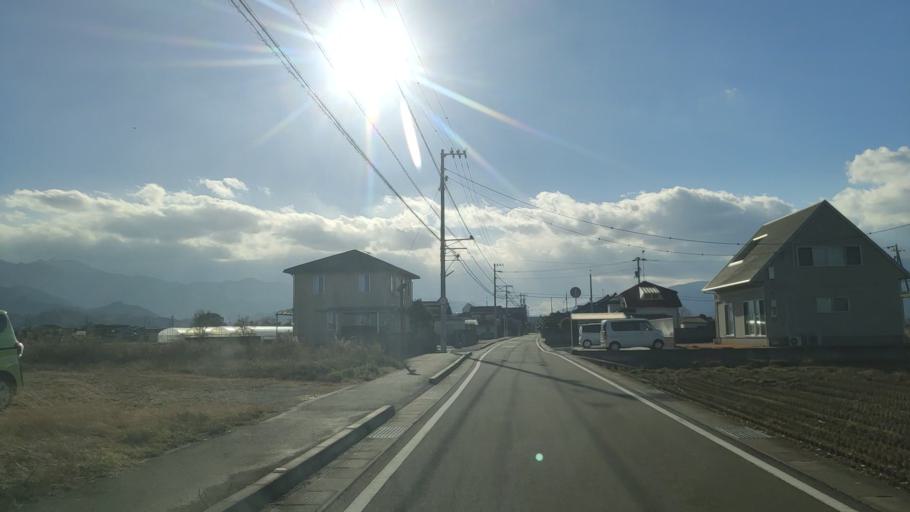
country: JP
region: Ehime
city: Saijo
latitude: 33.9154
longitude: 133.1034
